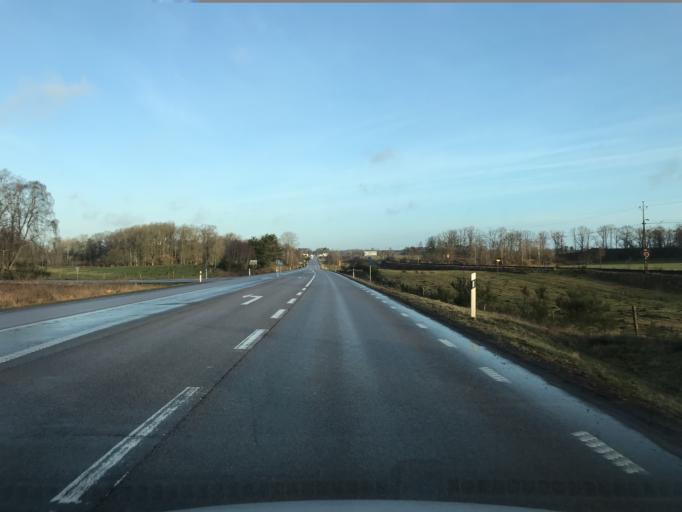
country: SE
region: Skane
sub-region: Hassleholms Kommun
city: Hassleholm
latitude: 56.1869
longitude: 13.7528
